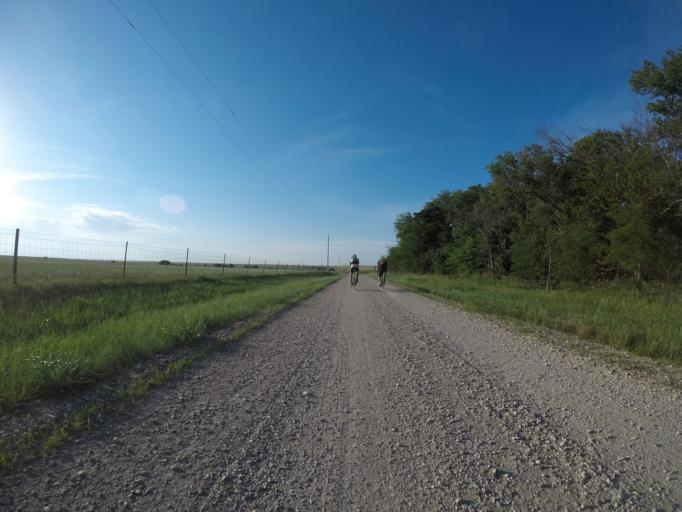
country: US
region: Kansas
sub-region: Riley County
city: Manhattan
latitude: 39.0140
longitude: -96.4919
